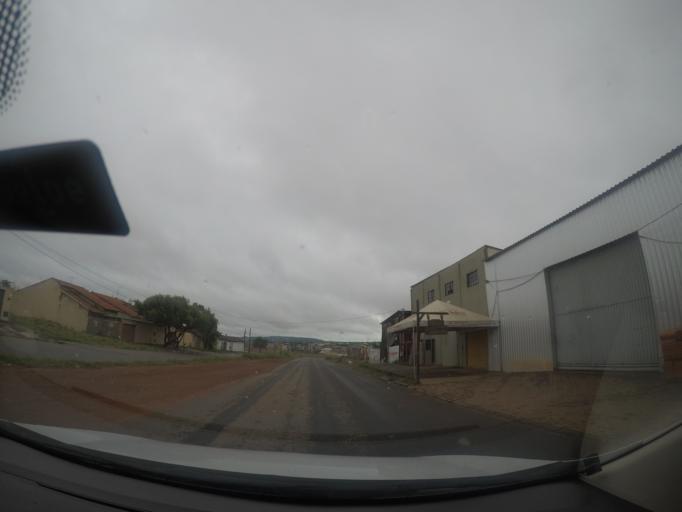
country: BR
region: Goias
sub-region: Goiania
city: Goiania
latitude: -16.7525
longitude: -49.3198
